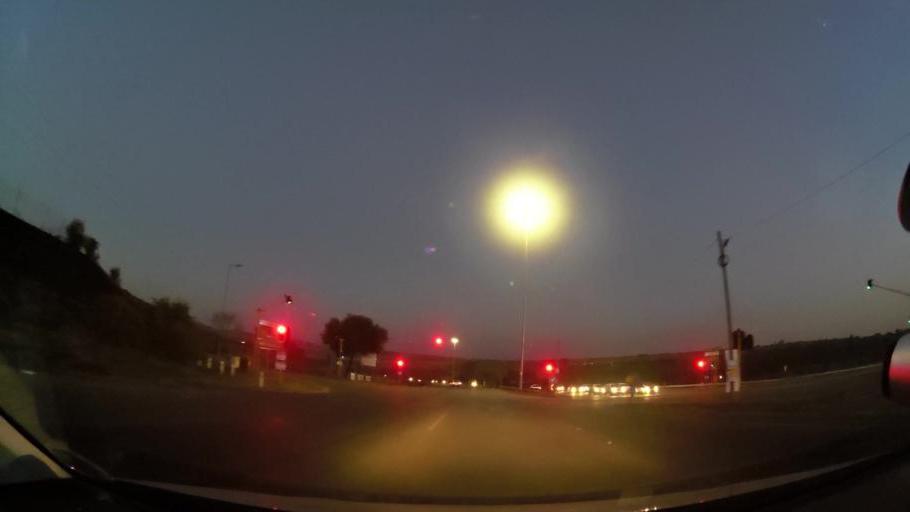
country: ZA
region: Gauteng
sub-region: City of Tshwane Metropolitan Municipality
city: Pretoria
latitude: -25.7788
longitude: 28.1701
